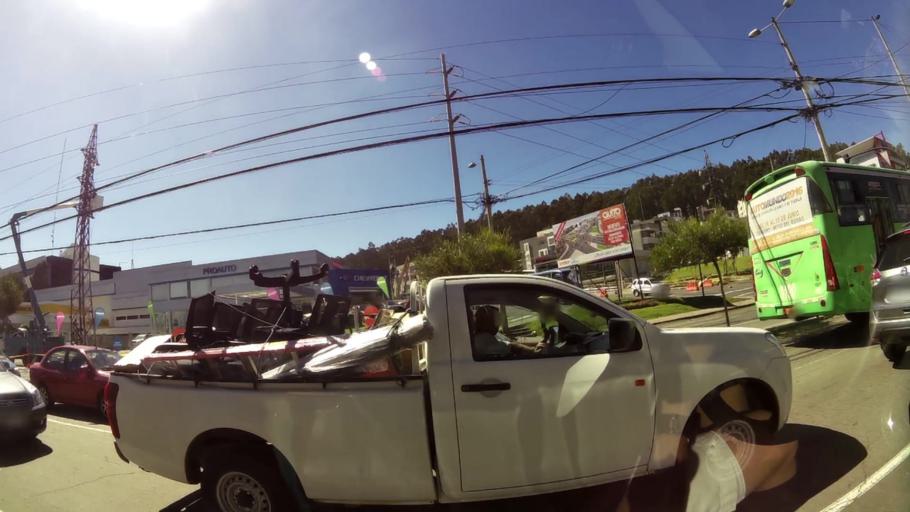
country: EC
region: Pichincha
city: Quito
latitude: -0.1656
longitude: -78.4684
